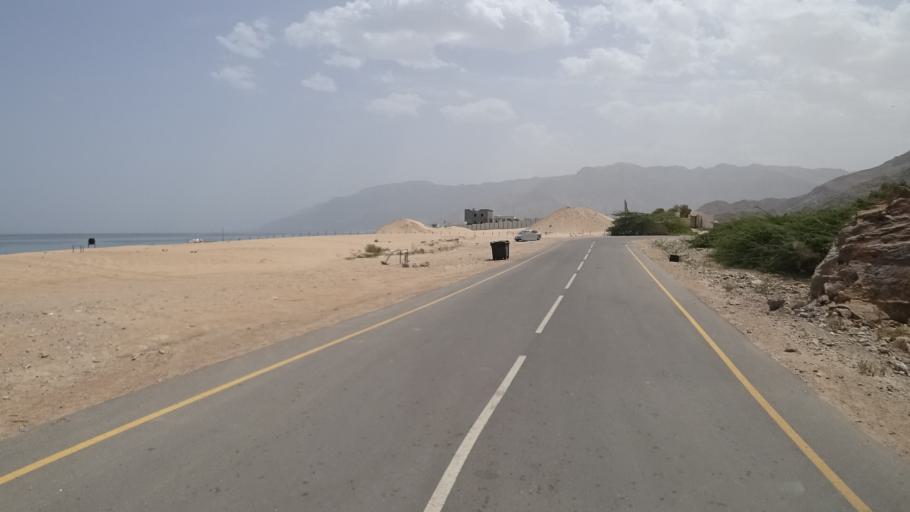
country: OM
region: Muhafazat Masqat
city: Muscat
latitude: 23.4391
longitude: 58.7808
